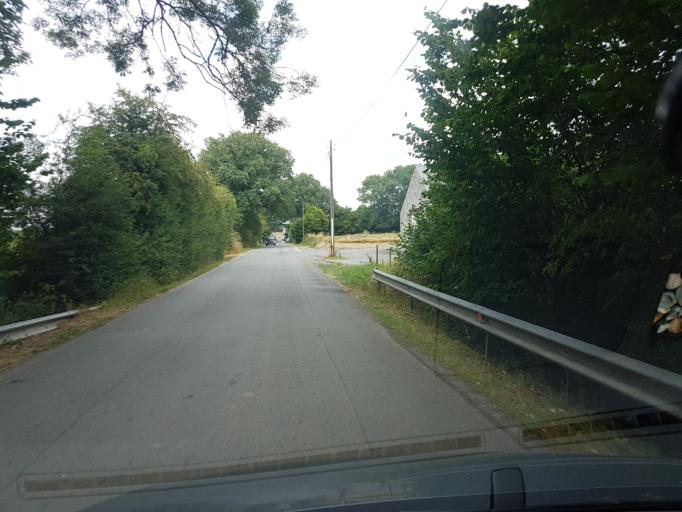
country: BE
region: Wallonia
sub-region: Province du Luxembourg
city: Manhay
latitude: 50.2889
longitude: 5.6729
